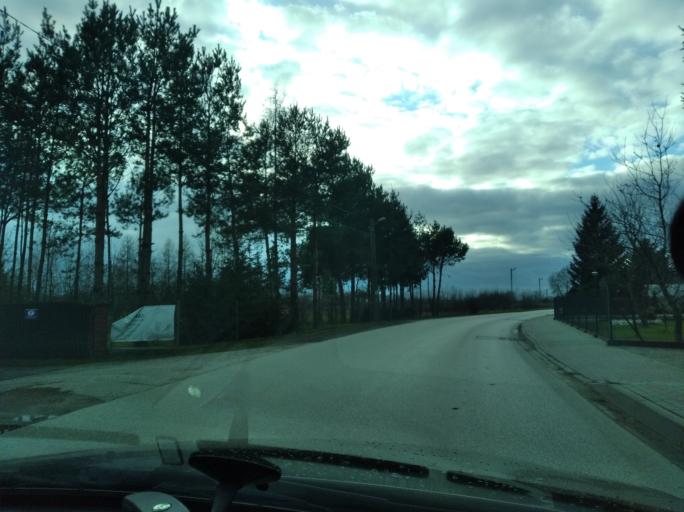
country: PL
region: Subcarpathian Voivodeship
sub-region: Powiat lancucki
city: Czarna
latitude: 50.1153
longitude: 22.2262
